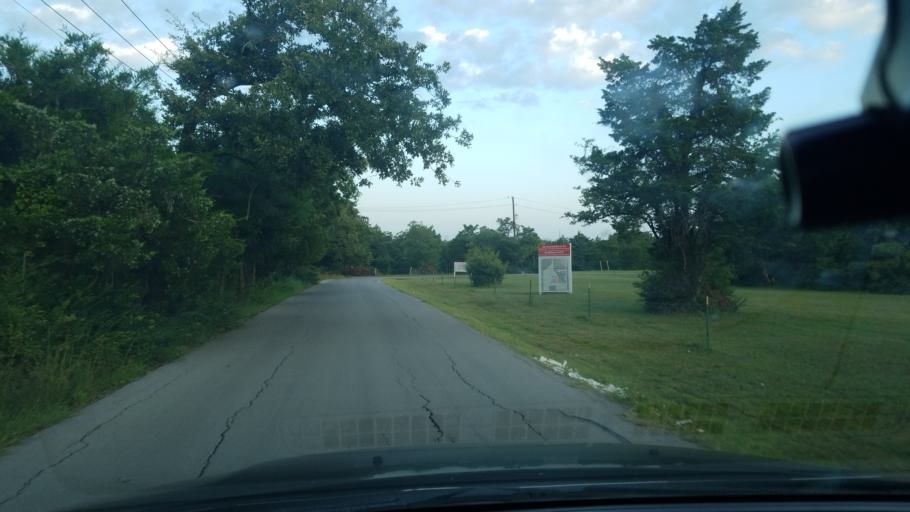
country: US
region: Texas
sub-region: Dallas County
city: Balch Springs
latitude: 32.7311
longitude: -96.6586
